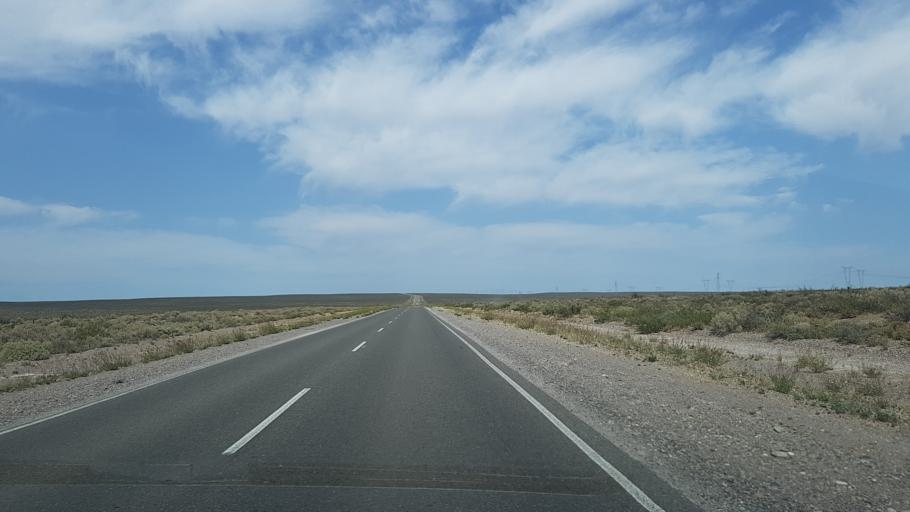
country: AR
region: Neuquen
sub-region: Departamento de Picun Leufu
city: Picun Leufu
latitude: -39.7181
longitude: -69.5349
